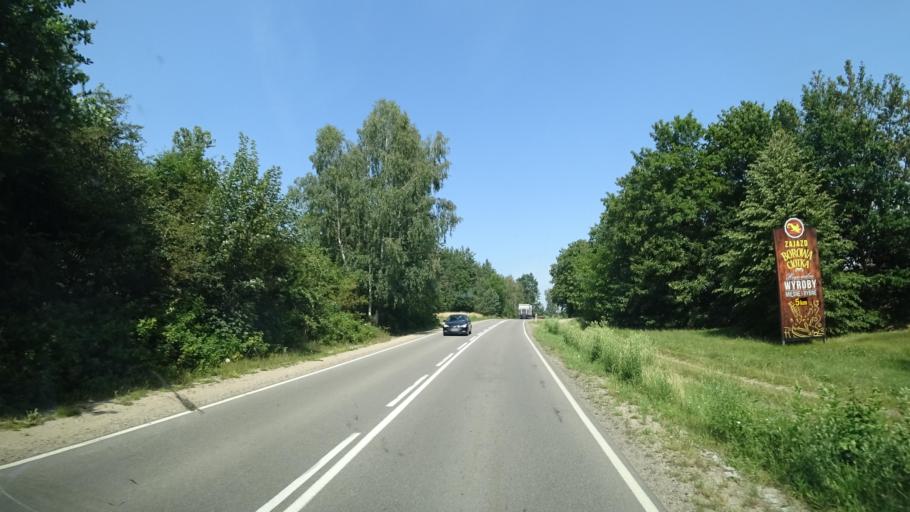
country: PL
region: Pomeranian Voivodeship
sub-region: Powiat koscierski
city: Lipusz
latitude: 54.0484
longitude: 17.7977
